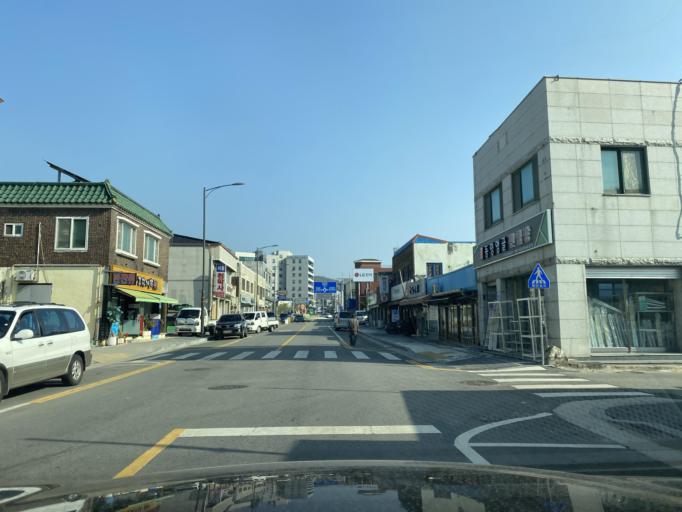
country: KR
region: Chungcheongnam-do
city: Yesan
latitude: 36.6784
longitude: 126.8416
